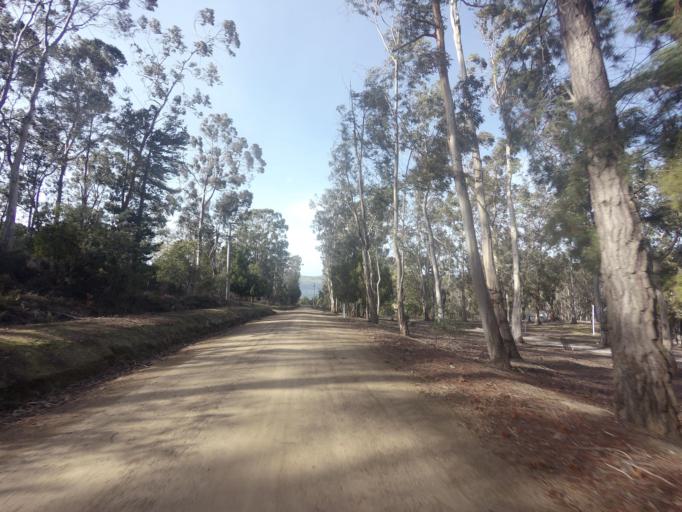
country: AU
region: Tasmania
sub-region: Kingborough
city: Kettering
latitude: -43.1182
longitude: 147.2676
